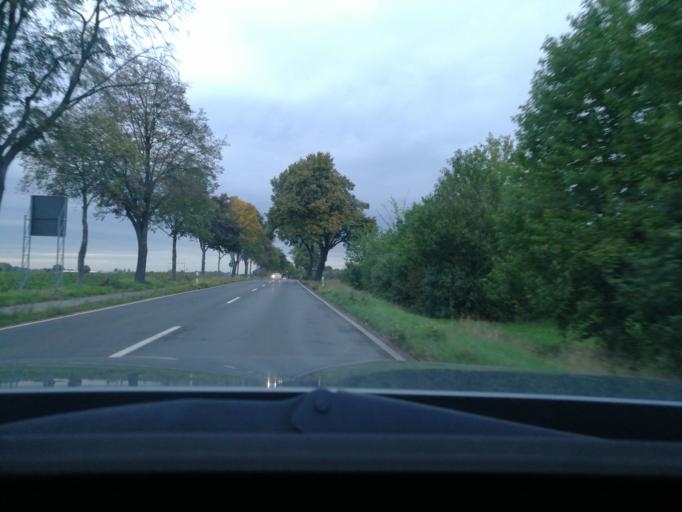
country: DE
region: North Rhine-Westphalia
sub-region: Regierungsbezirk Dusseldorf
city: Dormagen
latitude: 51.1202
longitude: 6.7670
